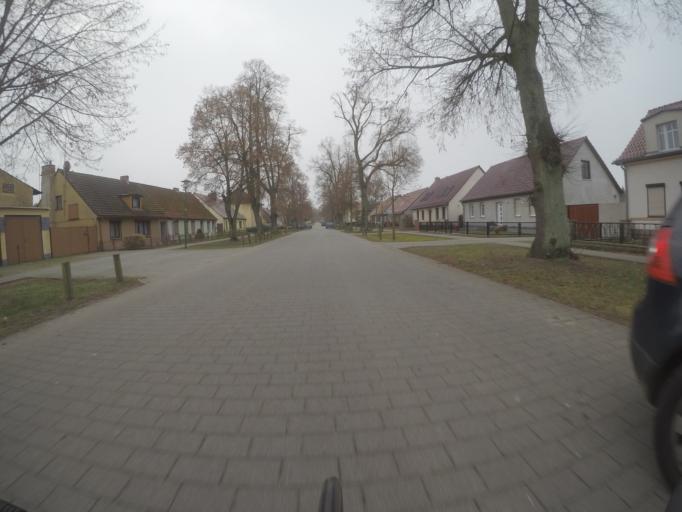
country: DE
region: Brandenburg
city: Marienwerder
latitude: 52.8409
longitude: 13.5999
